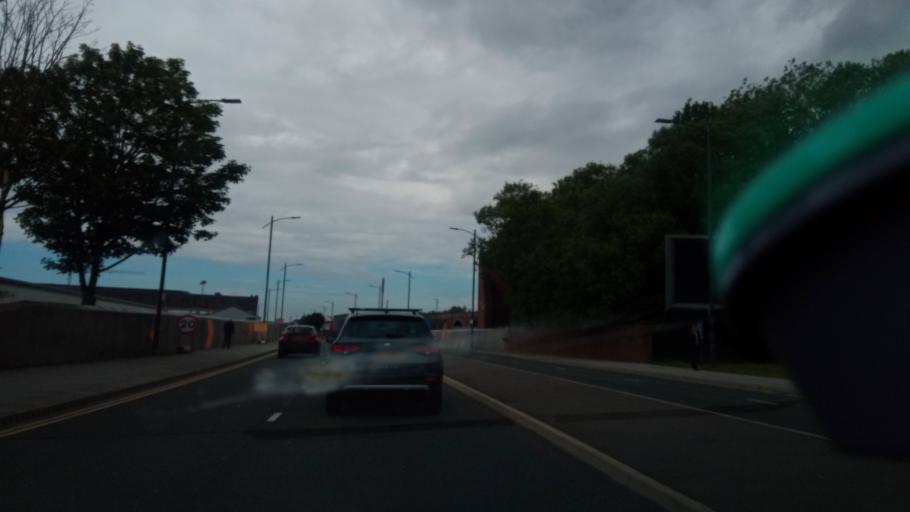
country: GB
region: England
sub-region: Liverpool
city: Liverpool
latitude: 53.4145
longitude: -2.9964
